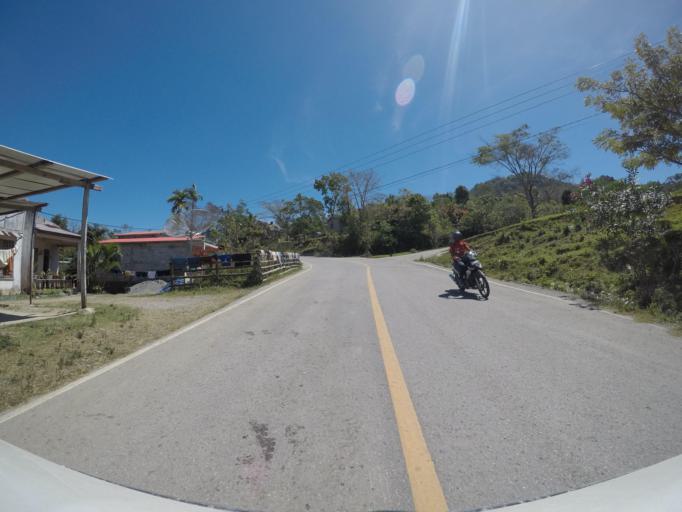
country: TL
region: Manatuto
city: Manatuto
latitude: -8.8262
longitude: 125.9848
